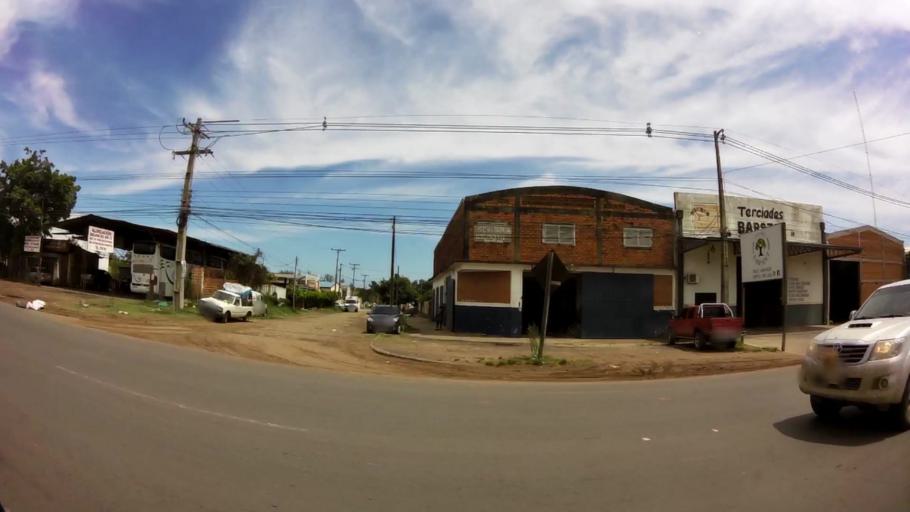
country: PY
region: Central
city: Colonia Mariano Roque Alonso
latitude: -25.2067
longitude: -57.5269
